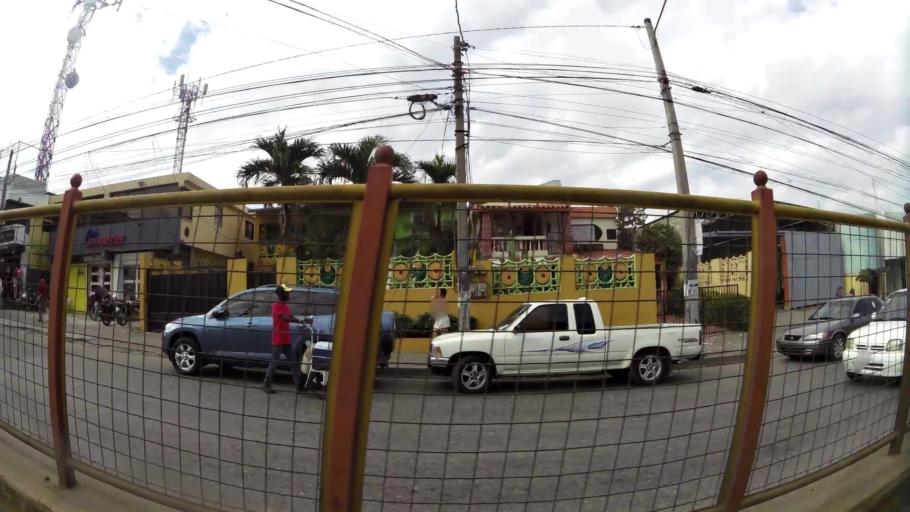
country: DO
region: Santiago
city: Santiago de los Caballeros
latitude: 19.4310
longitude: -70.6918
